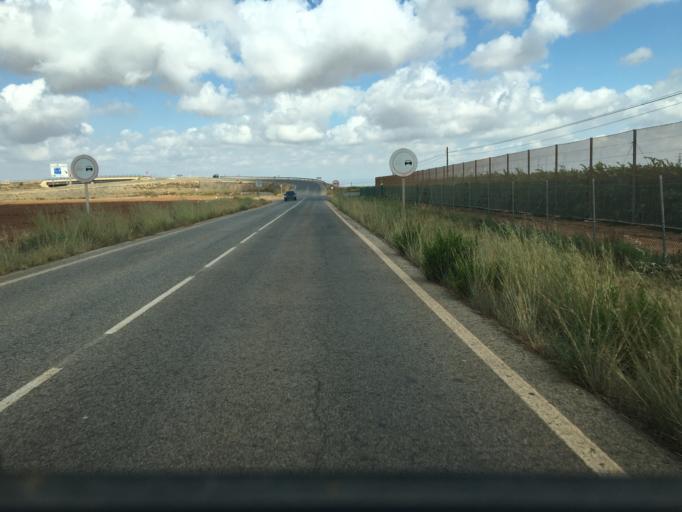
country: ES
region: Murcia
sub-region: Murcia
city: La Union
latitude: 37.6502
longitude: -0.8807
